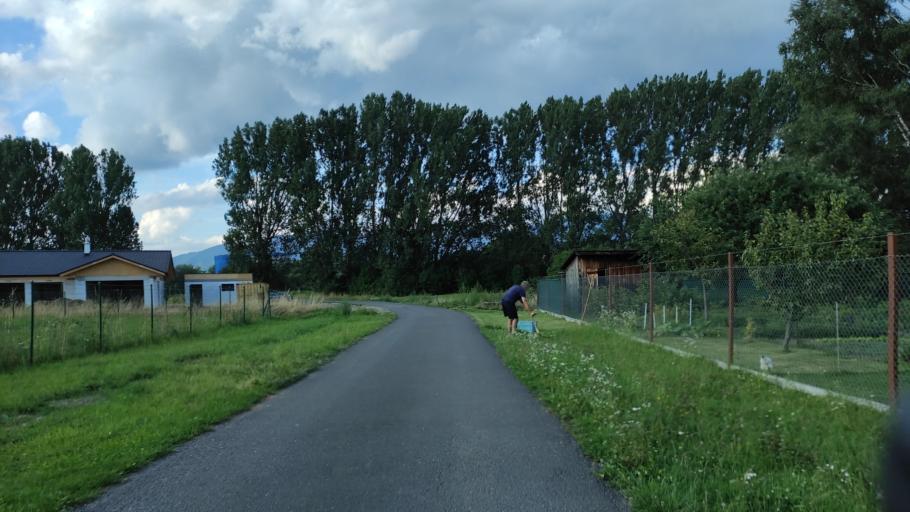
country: SK
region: Zilinsky
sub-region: Okres Liptovsky Mikulas
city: Liptovsky Mikulas
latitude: 49.0882
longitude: 19.5901
